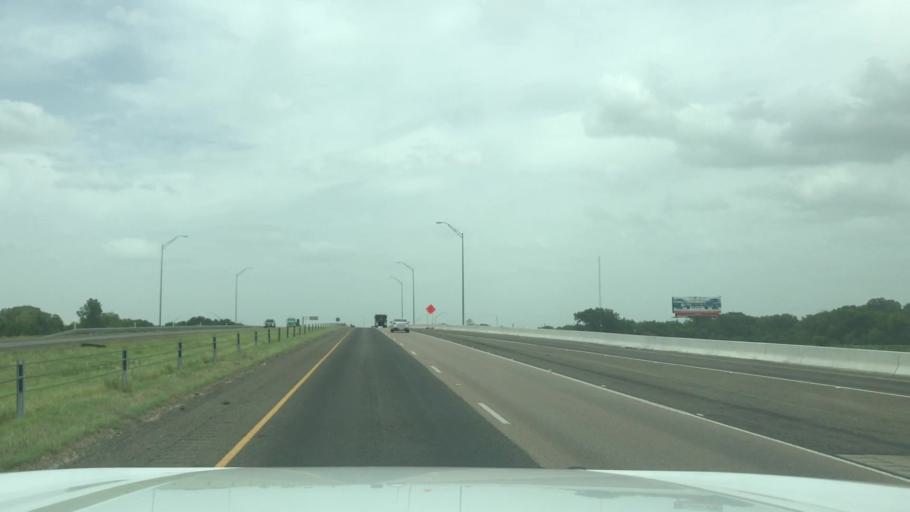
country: US
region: Texas
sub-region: McLennan County
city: Beverly
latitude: 31.5165
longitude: -97.0928
